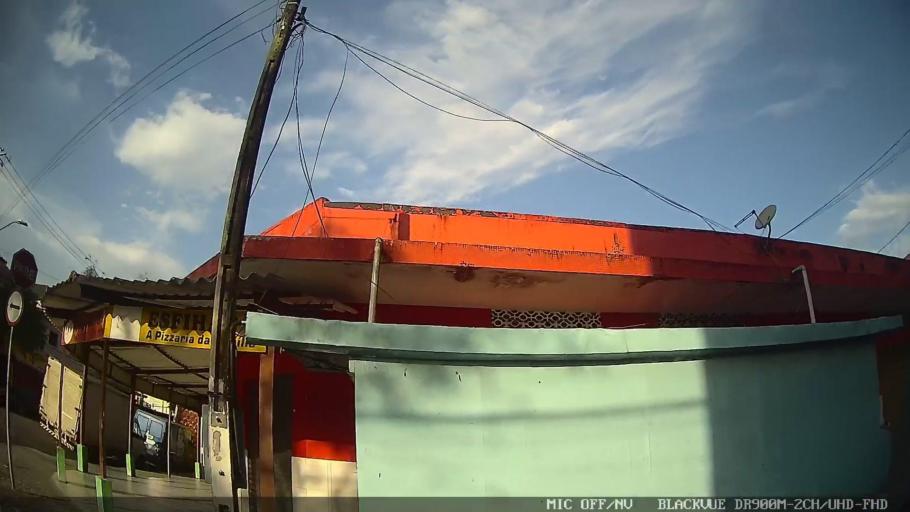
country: BR
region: Sao Paulo
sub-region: Cubatao
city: Cubatao
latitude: -23.8959
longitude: -46.4242
